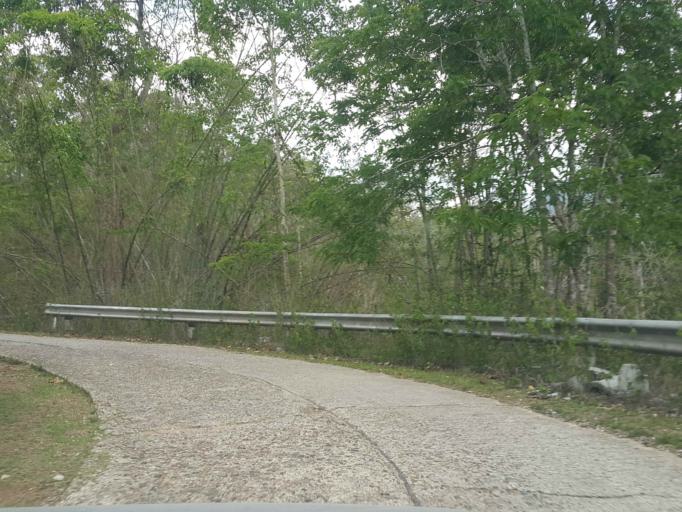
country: TH
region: Chiang Mai
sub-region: Amphoe Chiang Dao
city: Chiang Dao
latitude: 19.3791
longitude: 98.7674
